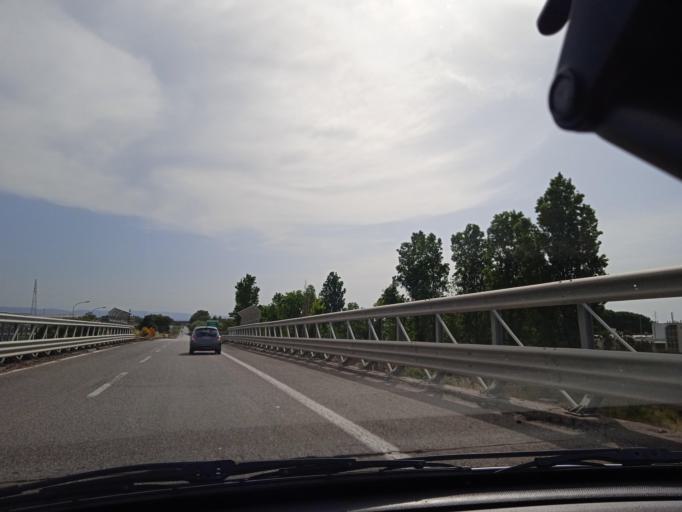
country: IT
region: Sicily
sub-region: Messina
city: San Filippo del Mela
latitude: 38.1913
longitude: 15.2720
